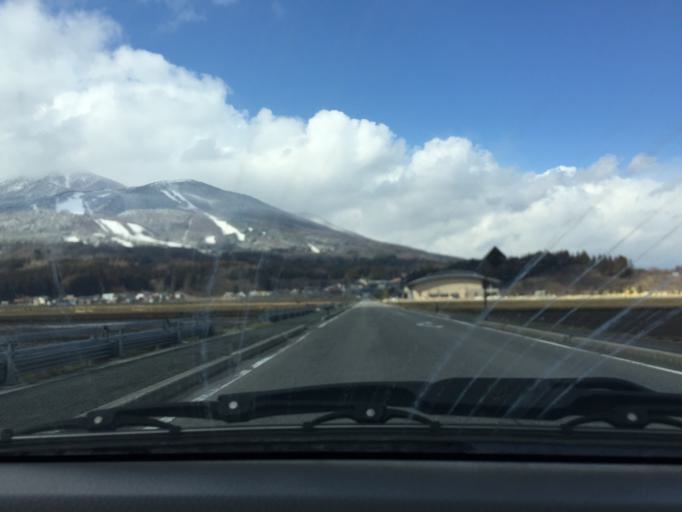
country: JP
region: Fukushima
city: Inawashiro
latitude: 37.5573
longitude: 140.0992
